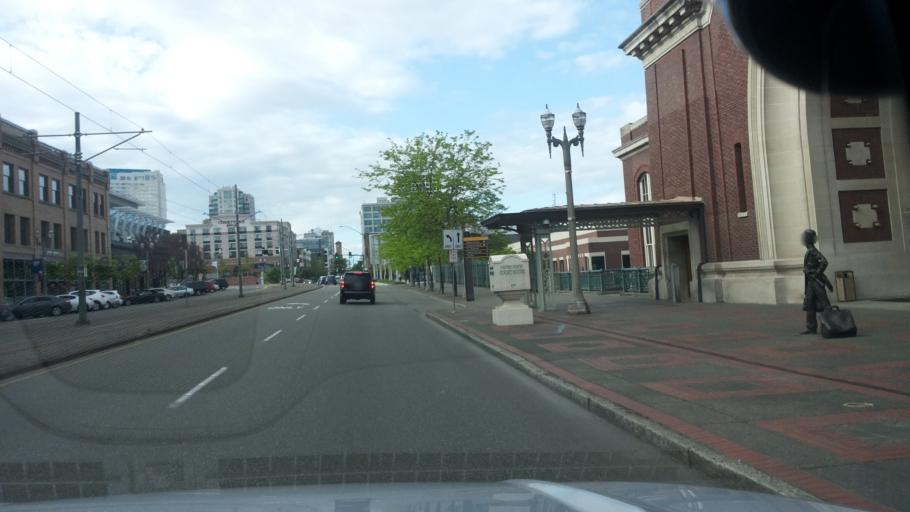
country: US
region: Washington
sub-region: Pierce County
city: Tacoma
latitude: 47.2459
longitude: -122.4368
